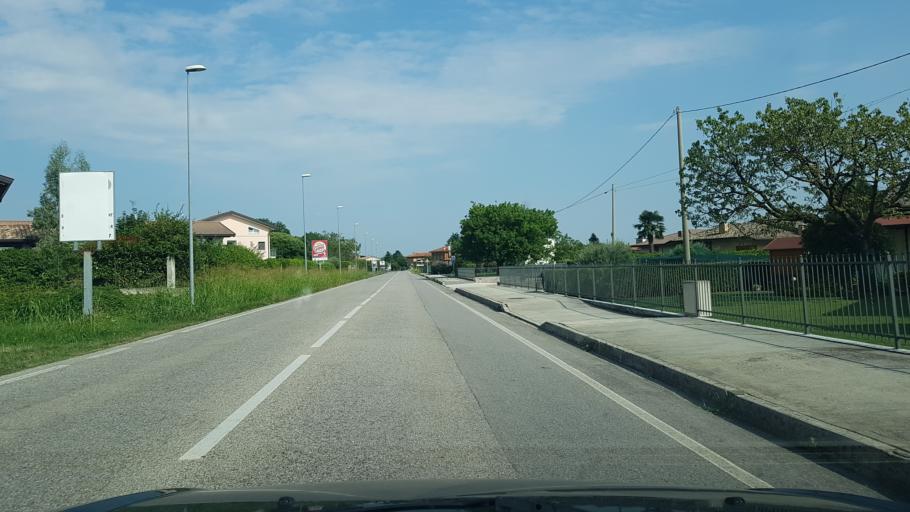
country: IT
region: Friuli Venezia Giulia
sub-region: Provincia di Udine
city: San Vito di Fagagna
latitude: 46.0884
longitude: 13.0506
